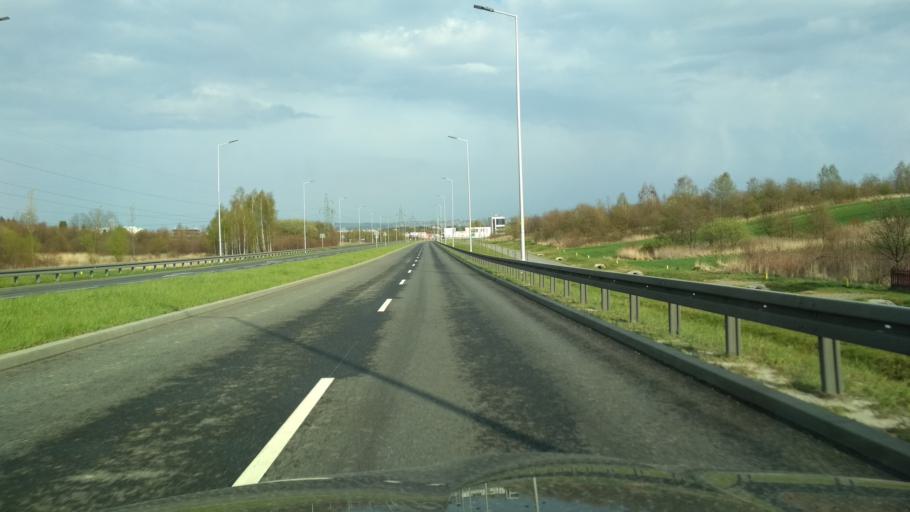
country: PL
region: Subcarpathian Voivodeship
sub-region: Powiat rzeszowski
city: Kielanowka
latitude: 50.0155
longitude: 21.9499
